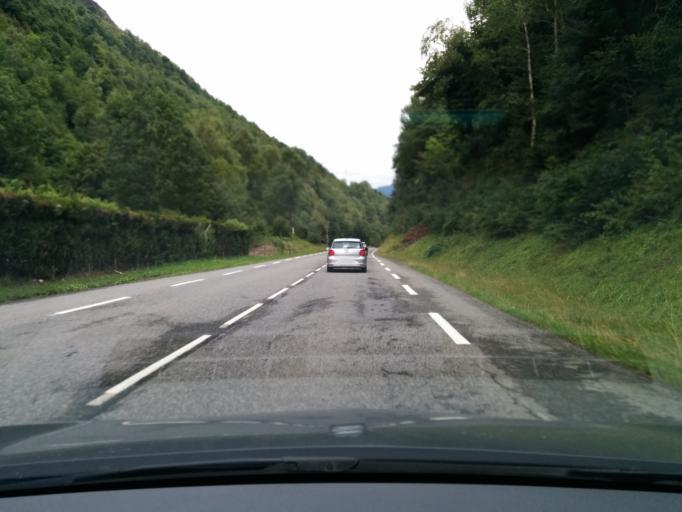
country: FR
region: Midi-Pyrenees
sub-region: Departement des Hautes-Pyrenees
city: Saint-Lary-Soulan
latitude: 42.8013
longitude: 0.2989
